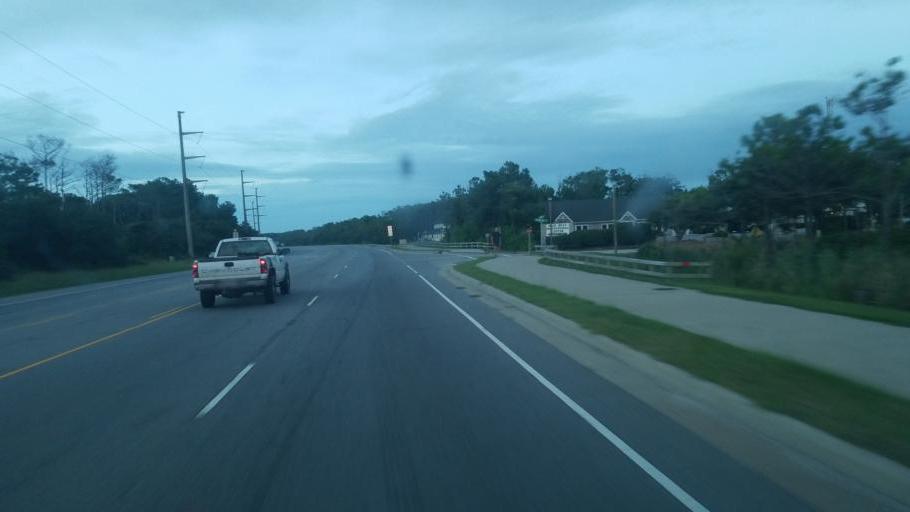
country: US
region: North Carolina
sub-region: Dare County
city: Nags Head
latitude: 35.9757
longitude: -75.6401
